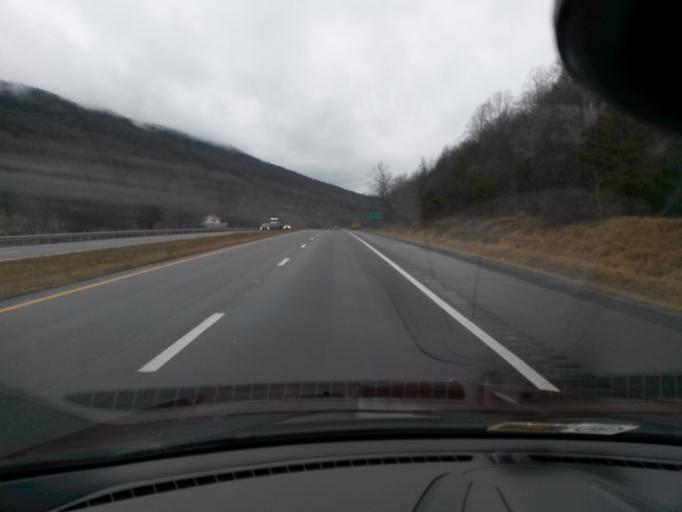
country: US
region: West Virginia
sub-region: Mercer County
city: Bluefield
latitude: 37.2797
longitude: -81.1396
